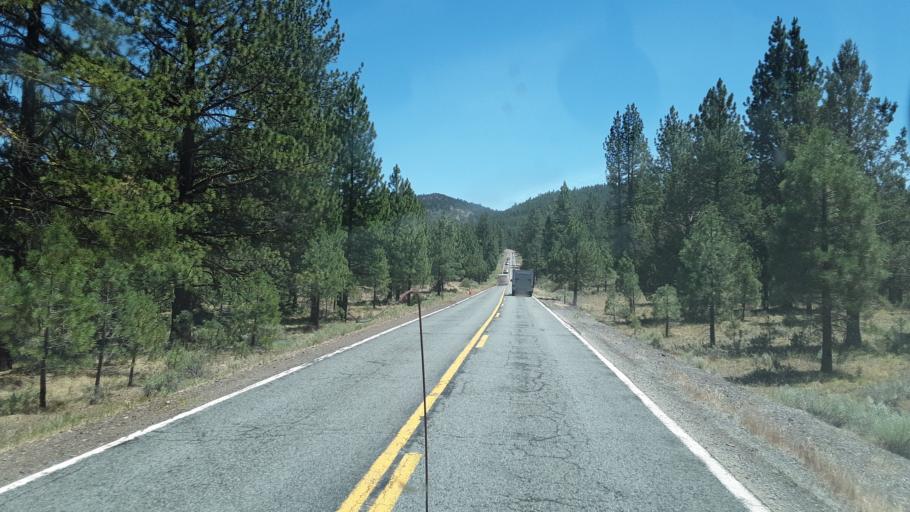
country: US
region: California
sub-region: Modoc County
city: Alturas
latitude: 40.9869
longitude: -120.7989
